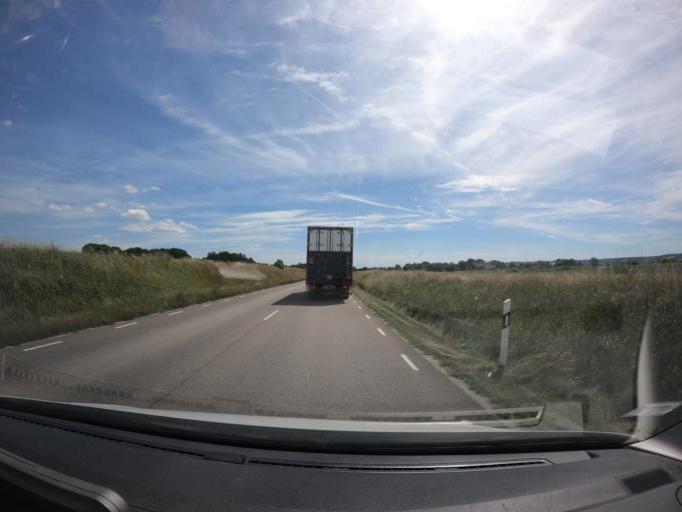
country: SE
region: Skane
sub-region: Astorps Kommun
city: Kvidinge
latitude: 56.1563
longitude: 13.0957
